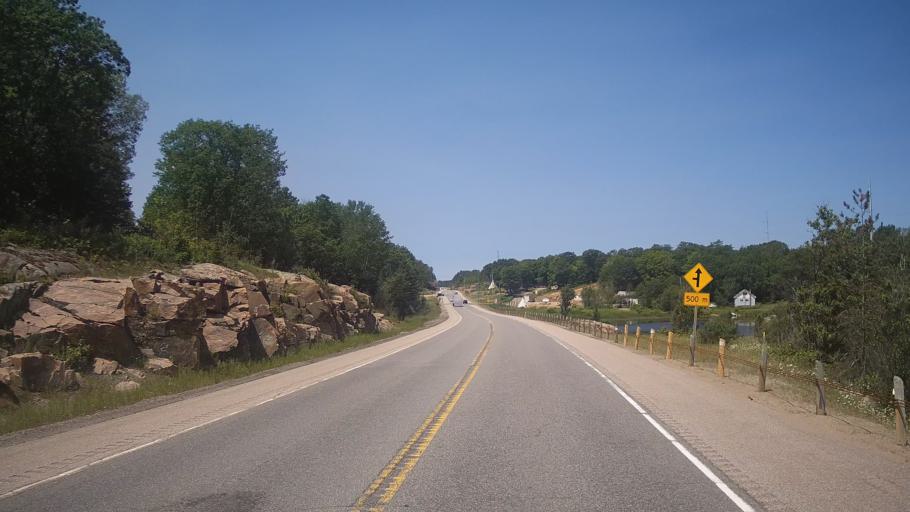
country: CA
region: Ontario
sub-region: Parry Sound District
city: Parry Sound
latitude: 45.5453
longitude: -80.2753
